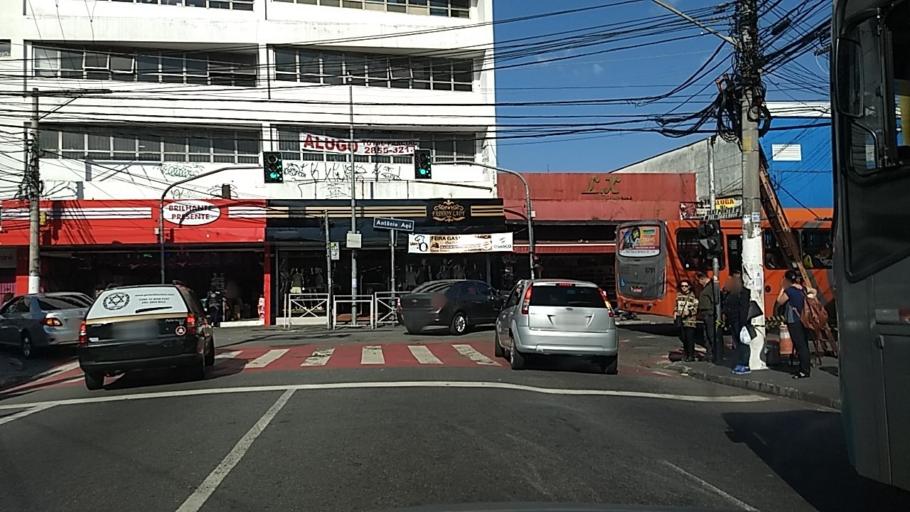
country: BR
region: Sao Paulo
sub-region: Osasco
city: Osasco
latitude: -23.5326
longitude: -46.7789
